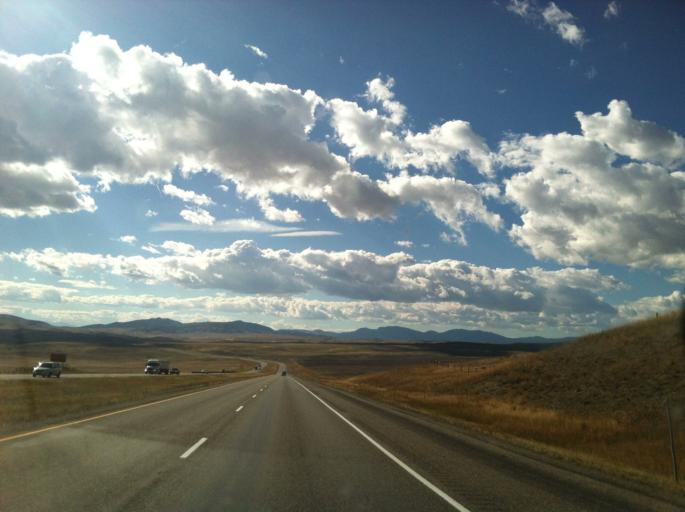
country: US
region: Montana
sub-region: Gallatin County
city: Three Forks
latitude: 45.9200
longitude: -111.6866
